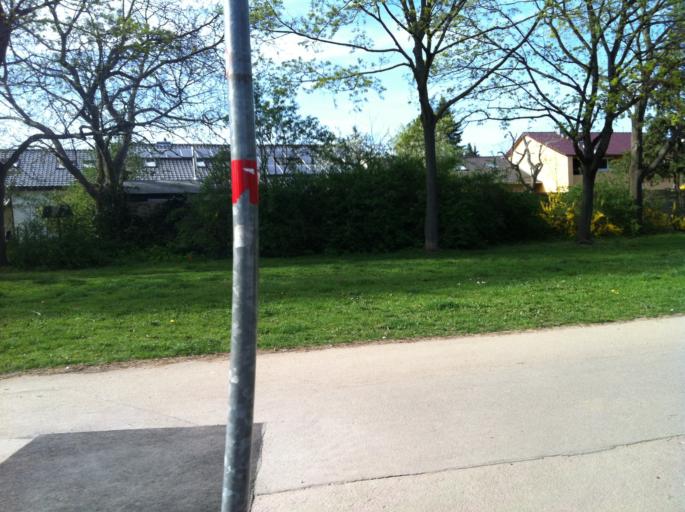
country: DE
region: Rheinland-Pfalz
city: Mainz
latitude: 49.9975
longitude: 8.2341
